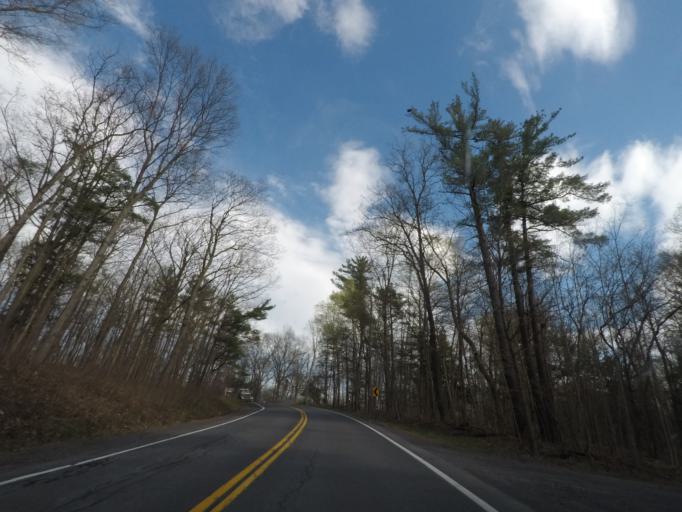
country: US
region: New York
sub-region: Albany County
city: Voorheesville
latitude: 42.5705
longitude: -73.9136
